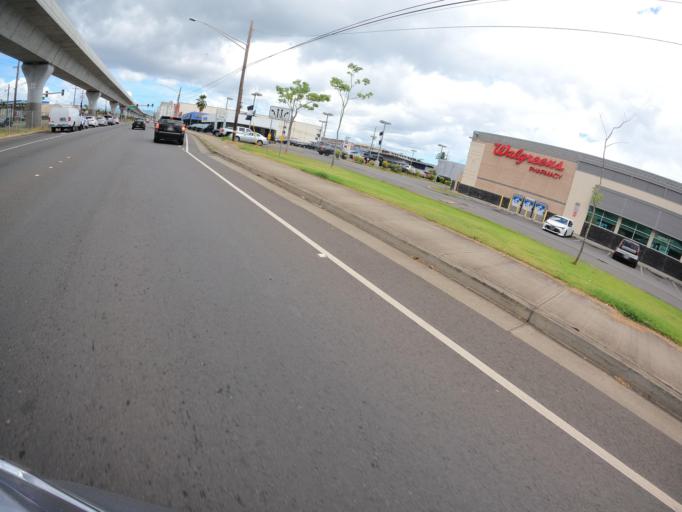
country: US
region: Hawaii
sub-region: Honolulu County
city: Waipahu
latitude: 21.3797
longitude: -158.0207
